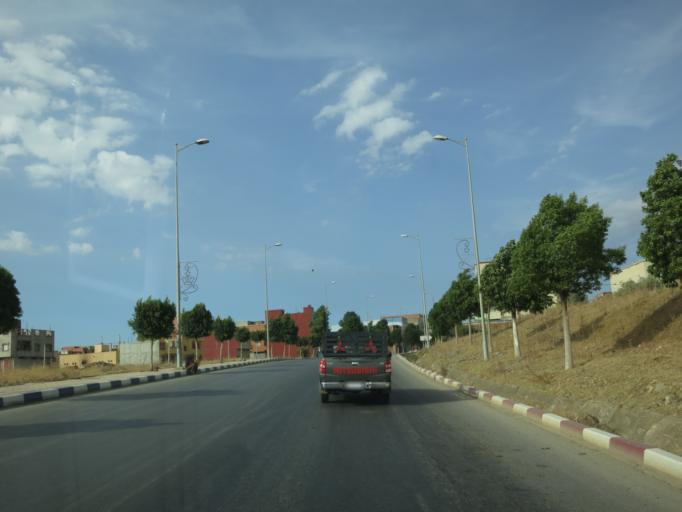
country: MA
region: Gharb-Chrarda-Beni Hssen
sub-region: Sidi-Kacem
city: Sidi Bousber
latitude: 34.4855
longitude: -5.5183
